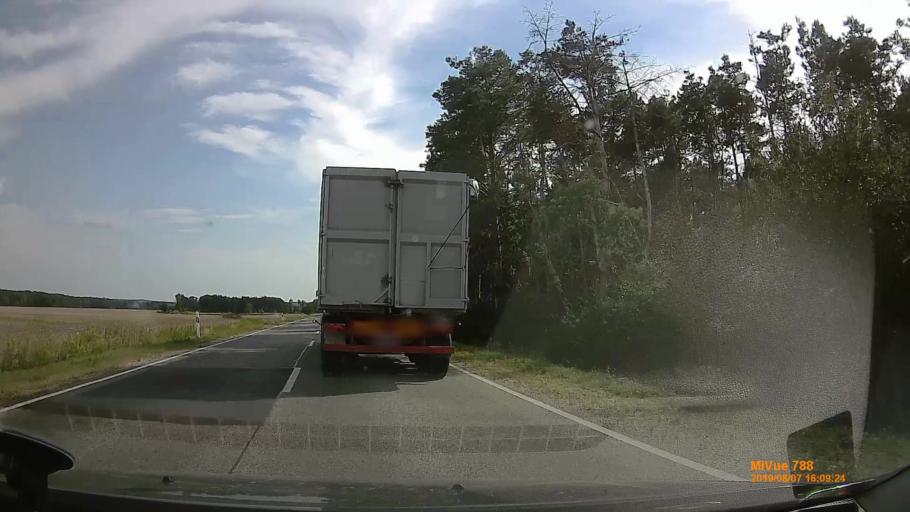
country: HU
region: Zala
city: Zalalovo
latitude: 46.8937
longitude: 16.6023
